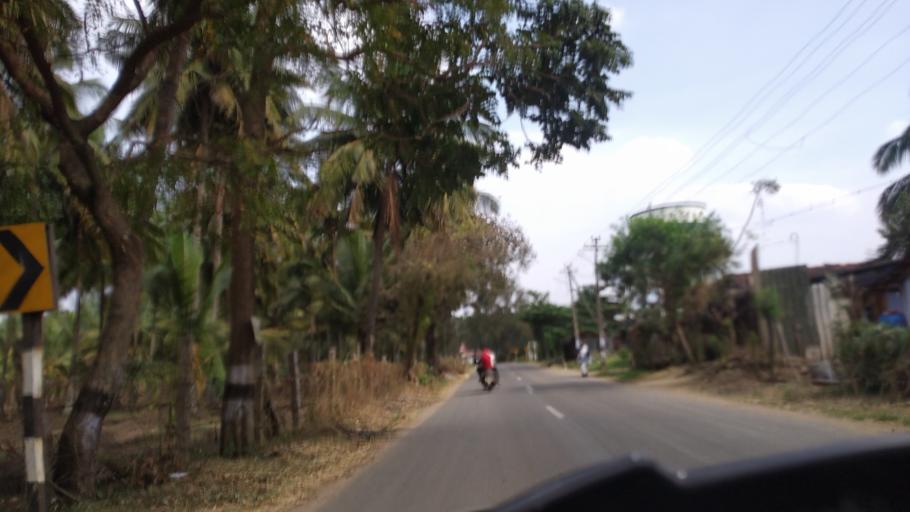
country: IN
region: Tamil Nadu
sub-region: Coimbatore
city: Perur
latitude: 10.9624
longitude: 76.7458
